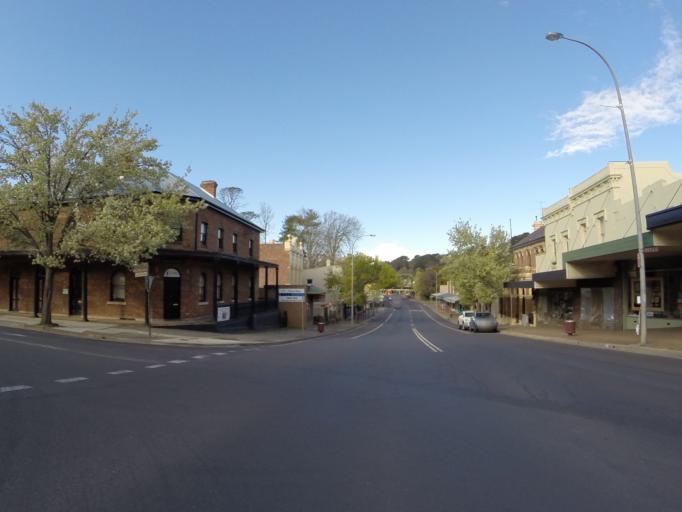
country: AU
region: New South Wales
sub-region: Wingecarribee
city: Moss Vale
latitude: -34.5513
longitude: 150.3678
